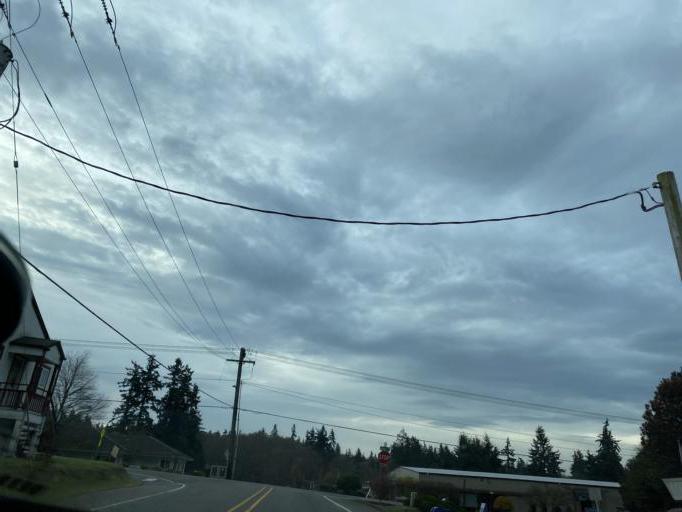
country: US
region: Washington
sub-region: Island County
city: Freeland
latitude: 48.0105
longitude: -122.5274
